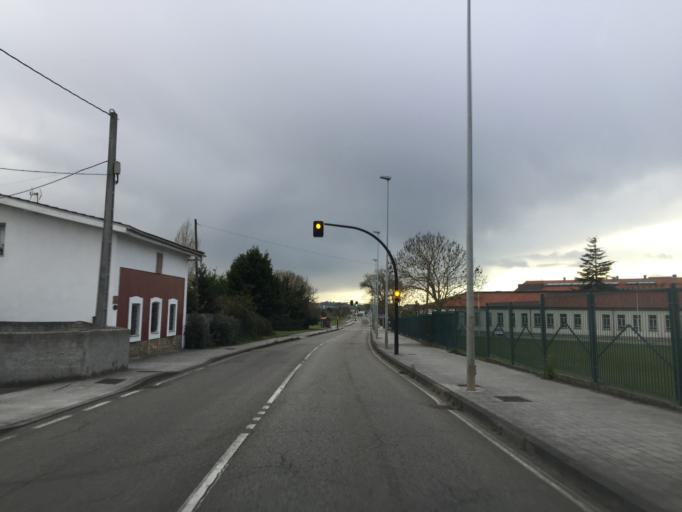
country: ES
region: Asturias
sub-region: Province of Asturias
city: Gijon
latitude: 43.5239
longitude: -5.6222
